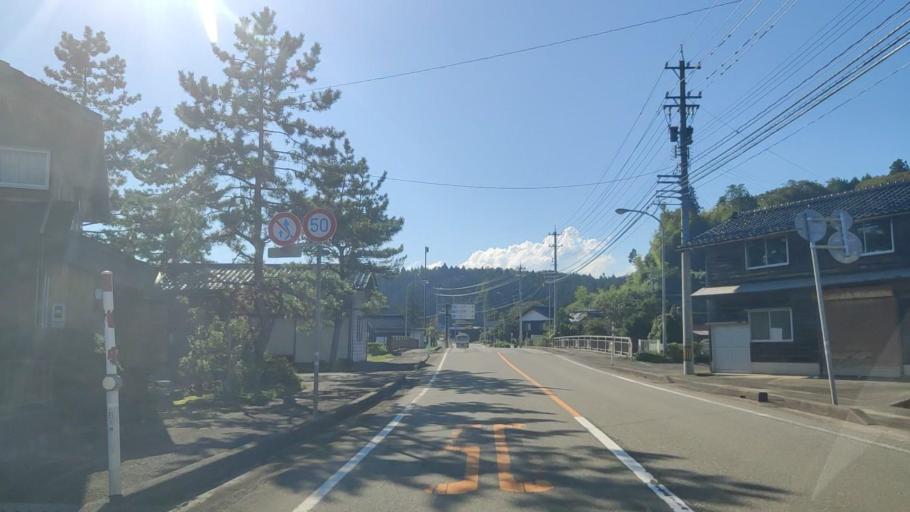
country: JP
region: Ishikawa
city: Nanao
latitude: 37.2366
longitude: 136.9627
